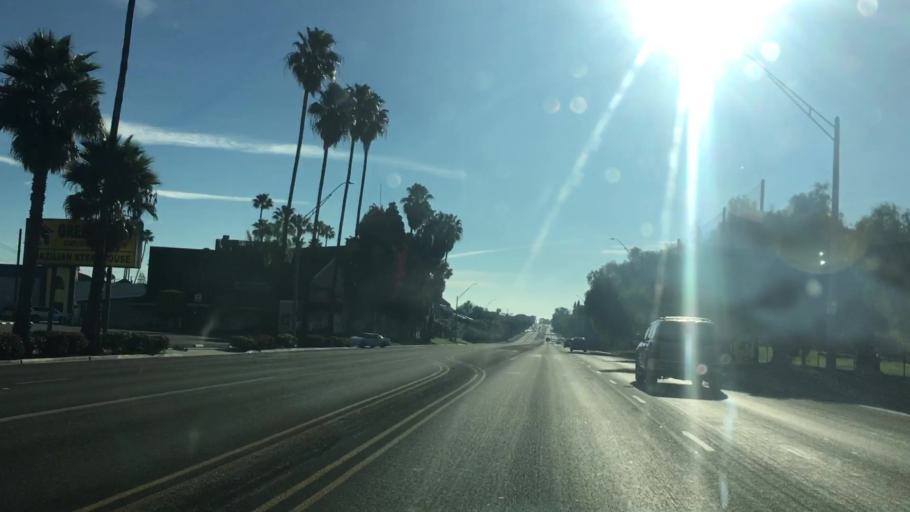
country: US
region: California
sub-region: Los Angeles County
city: Signal Hill
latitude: 33.7822
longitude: -118.1321
